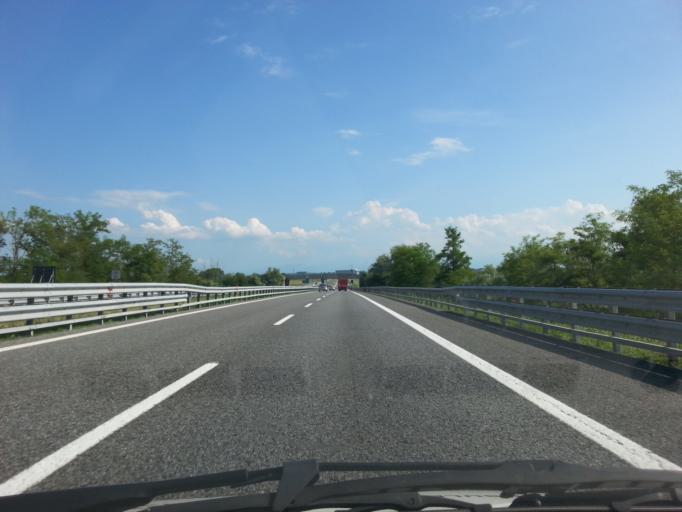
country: IT
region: Piedmont
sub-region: Provincia di Cuneo
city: Marene
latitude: 44.6947
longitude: 7.7657
